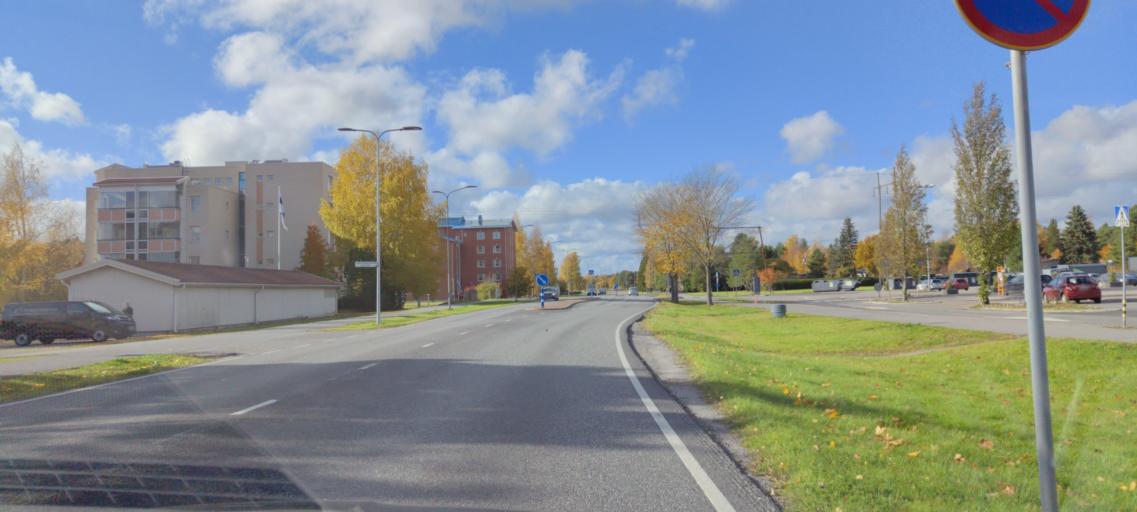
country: FI
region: Varsinais-Suomi
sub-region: Turku
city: Kaarina
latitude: 60.4071
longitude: 22.3614
